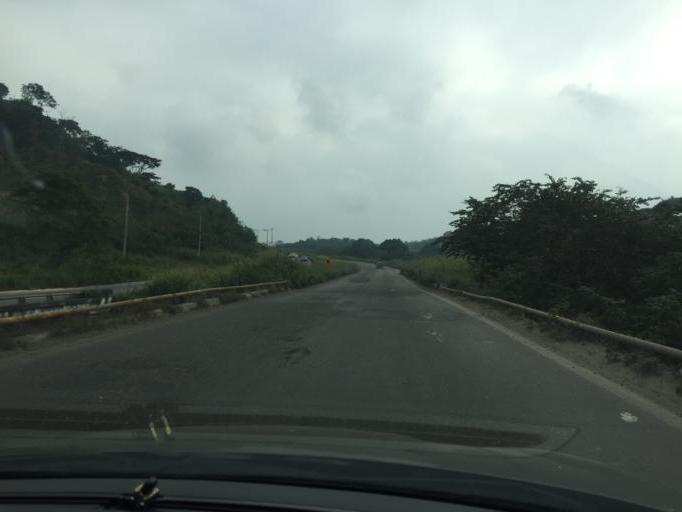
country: MX
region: Veracruz
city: Villa Nanchital
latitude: 18.0715
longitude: -94.3130
